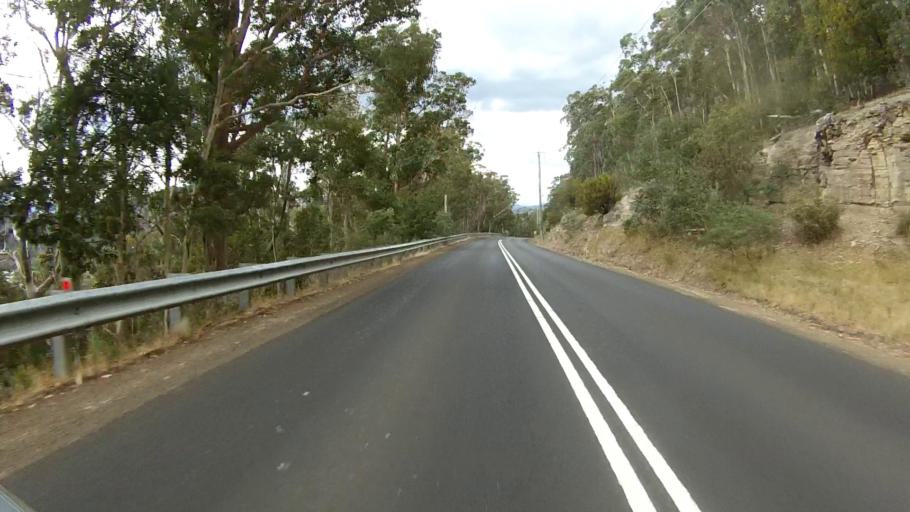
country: AU
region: Tasmania
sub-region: Hobart
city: Dynnyrne
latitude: -42.9061
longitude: 147.2757
